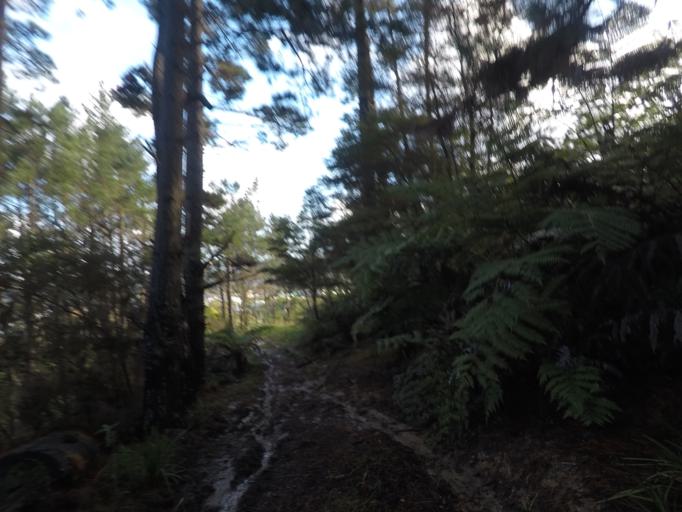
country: NZ
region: Auckland
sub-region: Auckland
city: Waitakere
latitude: -36.9066
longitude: 174.6444
